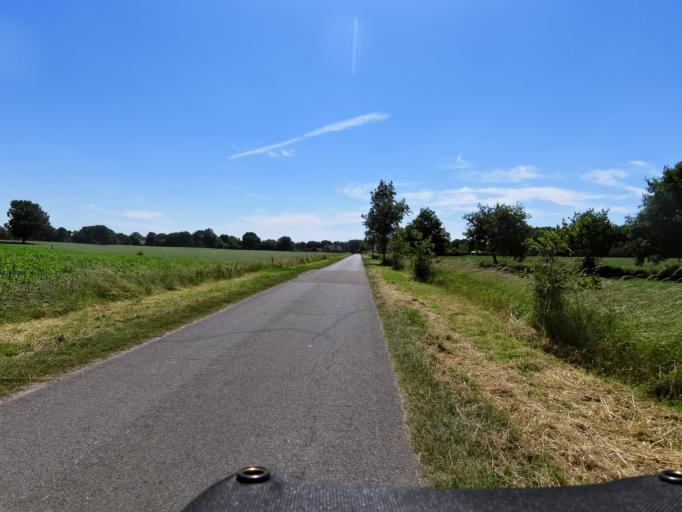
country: NL
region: Overijssel
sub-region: Gemeente Twenterand
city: Den Ham
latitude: 52.4978
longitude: 6.4030
